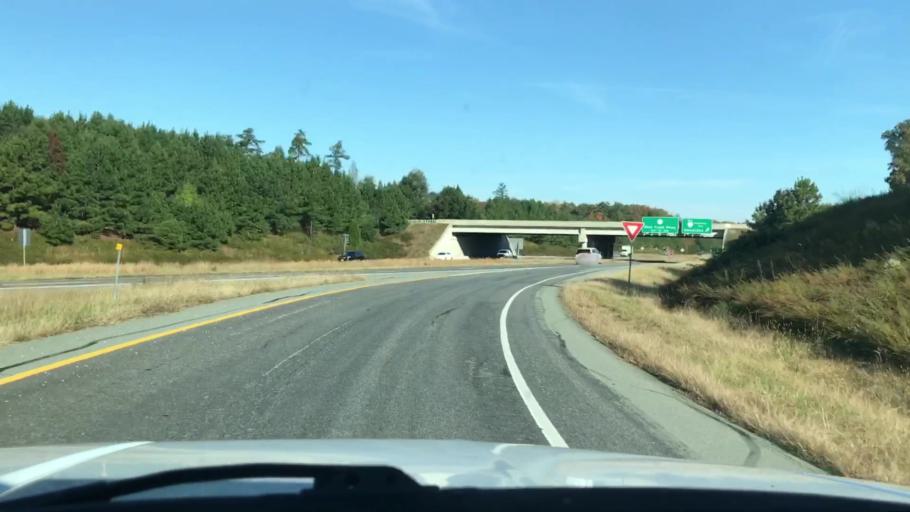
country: US
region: Virginia
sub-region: Henrico County
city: Short Pump
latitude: 37.5984
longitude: -77.6668
